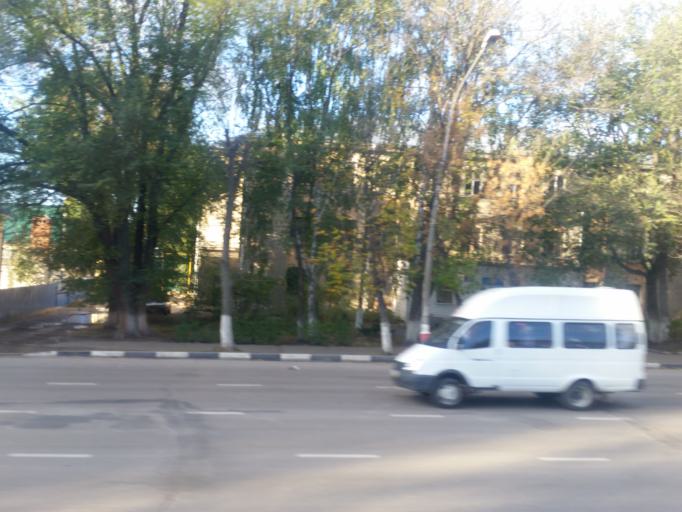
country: RU
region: Ulyanovsk
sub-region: Ulyanovskiy Rayon
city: Ulyanovsk
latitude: 54.3383
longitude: 48.3808
